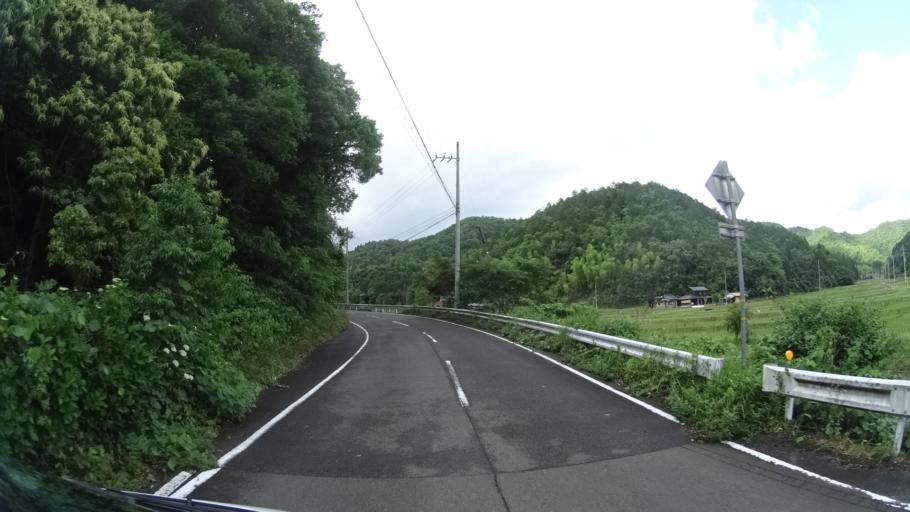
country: JP
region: Kyoto
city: Ayabe
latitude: 35.3815
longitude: 135.2138
